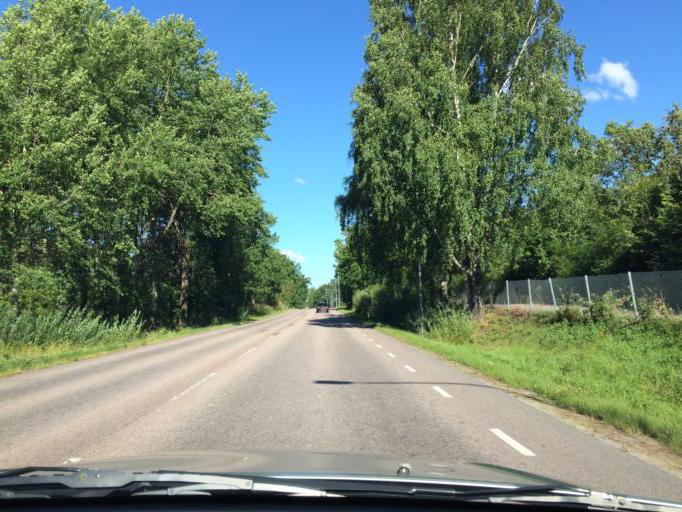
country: SE
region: Vaestmanland
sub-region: Vasteras
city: Vasteras
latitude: 59.6033
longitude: 16.5870
